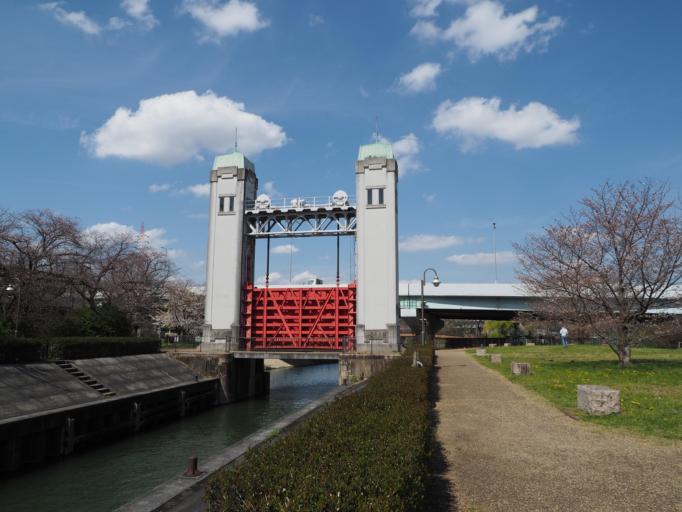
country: JP
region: Kyoto
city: Uji
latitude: 34.9233
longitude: 135.7562
